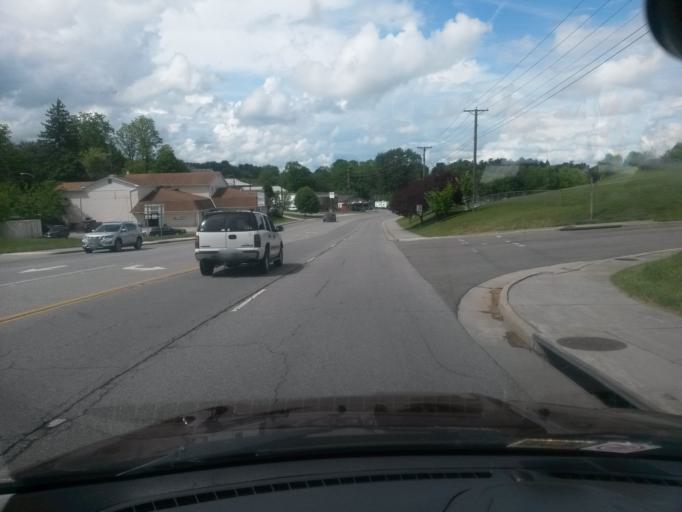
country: US
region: Virginia
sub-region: Montgomery County
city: Christiansburg
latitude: 37.1282
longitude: -80.4165
